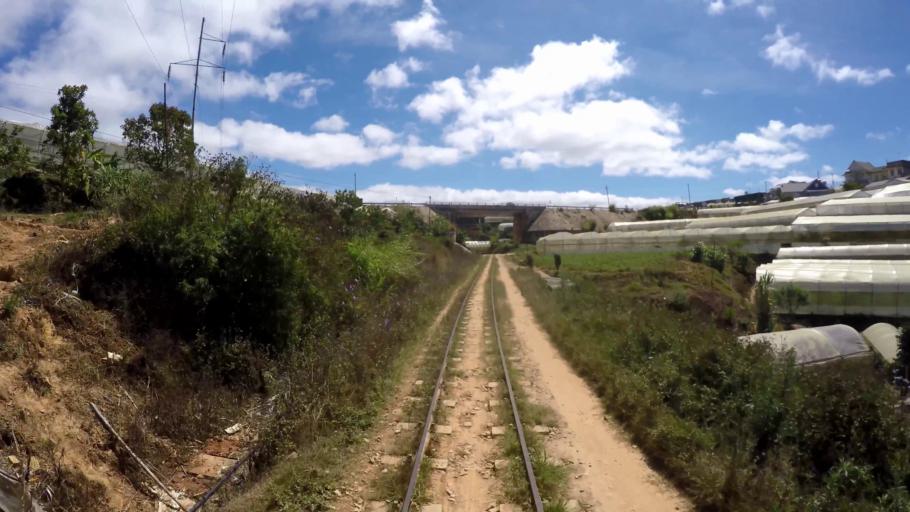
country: VN
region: Lam Dong
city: Da Lat
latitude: 11.9520
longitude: 108.4748
